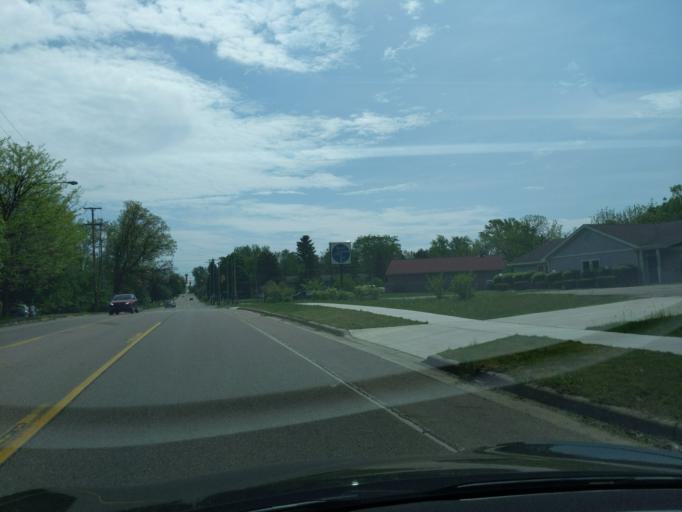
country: US
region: Michigan
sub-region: Ingham County
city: Holt
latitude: 42.6547
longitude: -84.5251
